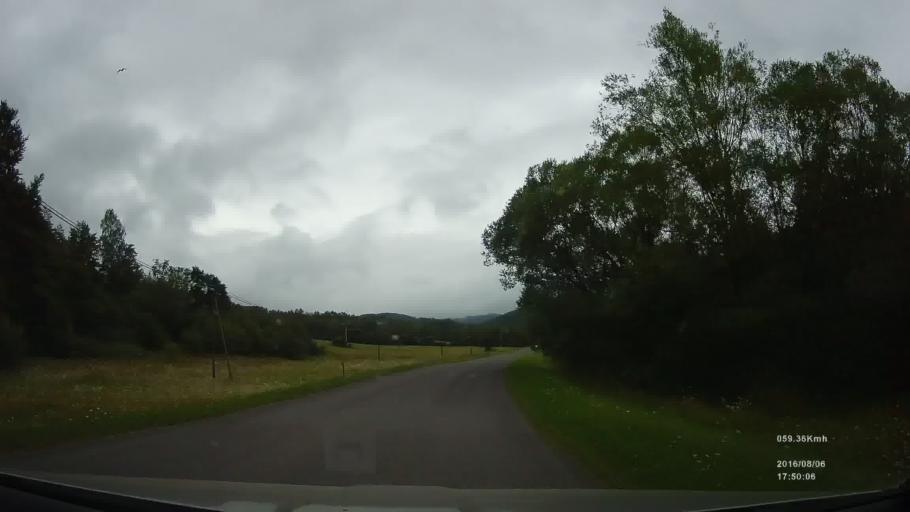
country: SK
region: Presovsky
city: Svidnik
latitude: 49.3885
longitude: 21.5659
